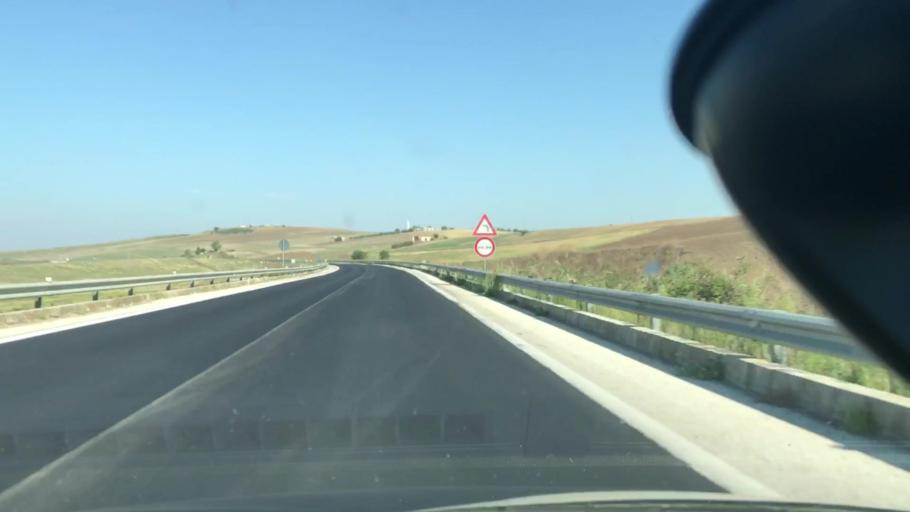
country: IT
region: Apulia
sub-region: Provincia di Barletta - Andria - Trani
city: Spinazzola
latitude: 40.9165
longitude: 16.1020
